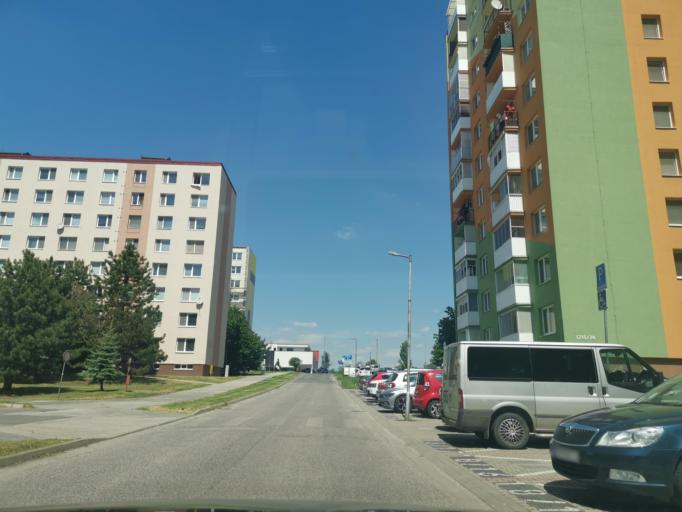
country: SK
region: Trnavsky
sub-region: Okres Senica
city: Senica
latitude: 48.6862
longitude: 17.3730
